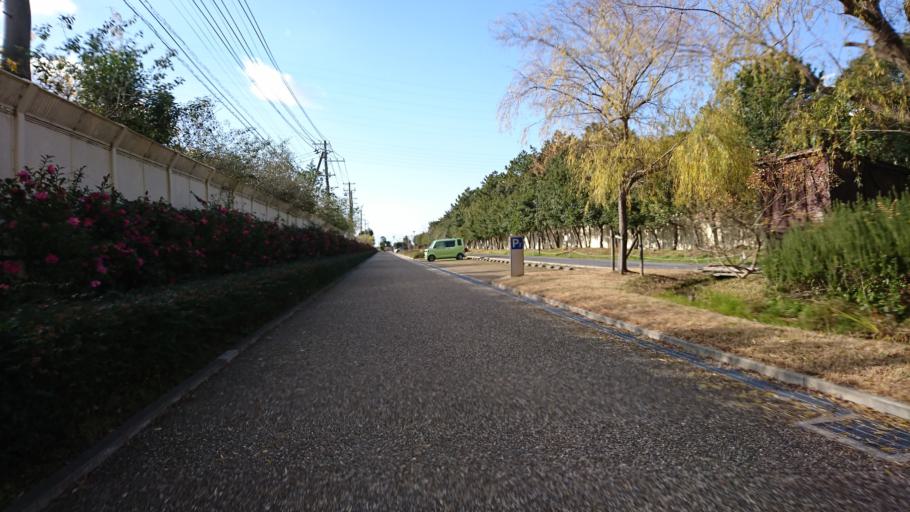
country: JP
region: Hyogo
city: Kakogawacho-honmachi
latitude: 34.7479
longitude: 134.7795
